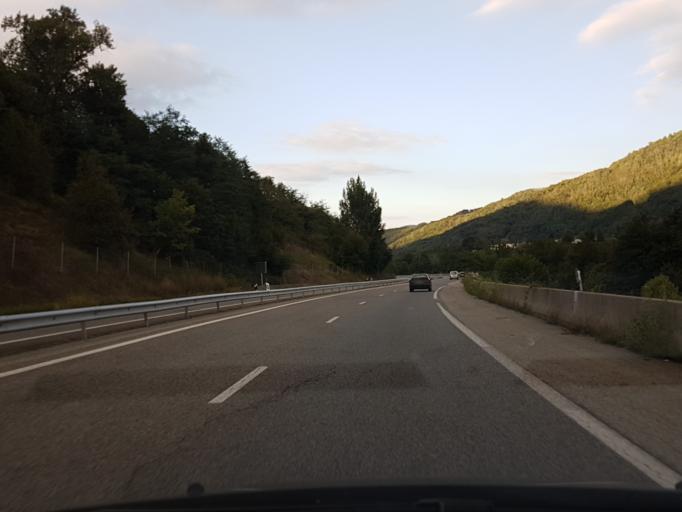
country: FR
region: Midi-Pyrenees
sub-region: Departement de l'Ariege
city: Mercus-Garrabet
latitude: 42.8853
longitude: 1.6243
